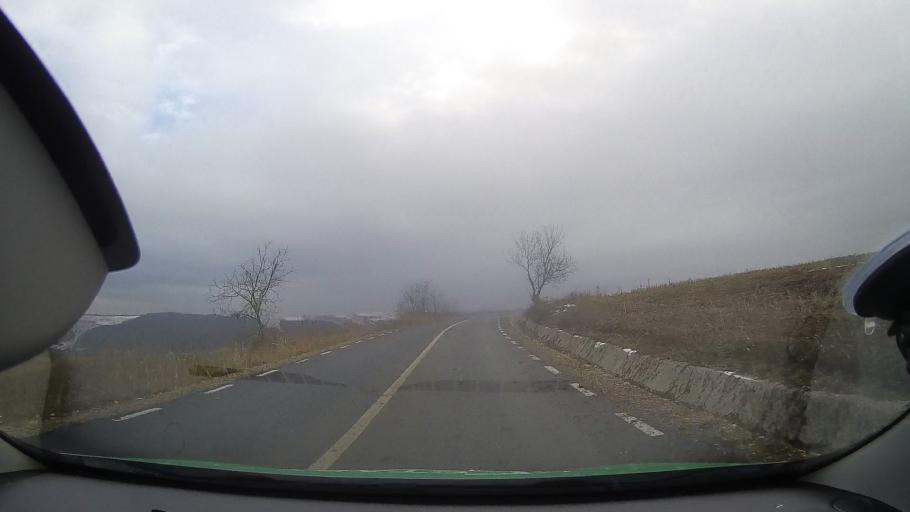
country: RO
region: Alba
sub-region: Comuna Farau
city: Farau
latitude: 46.3981
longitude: 24.0209
